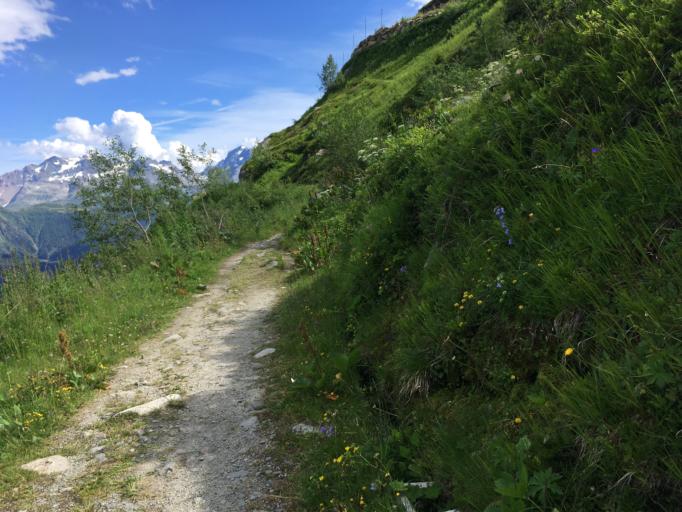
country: CH
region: Valais
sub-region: Goms District
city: Fiesch
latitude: 46.4231
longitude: 8.1102
